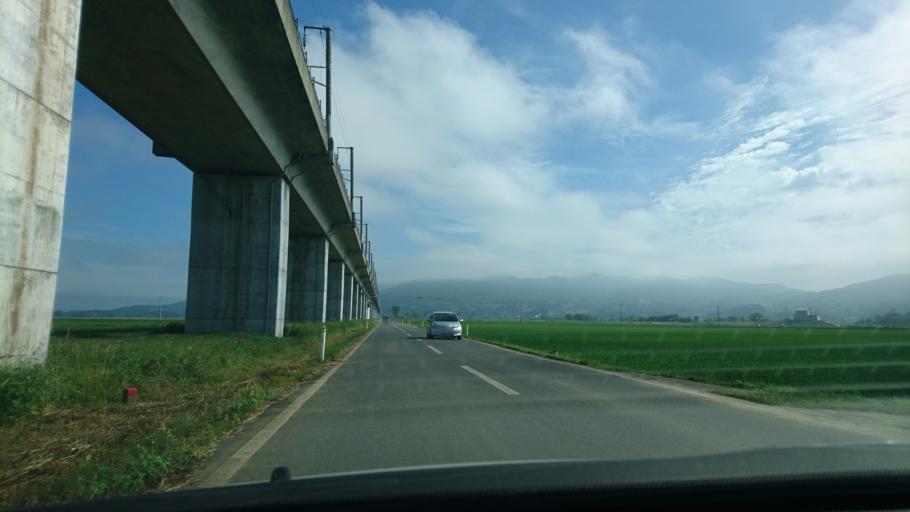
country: JP
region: Iwate
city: Ichinoseki
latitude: 38.9535
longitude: 141.1495
